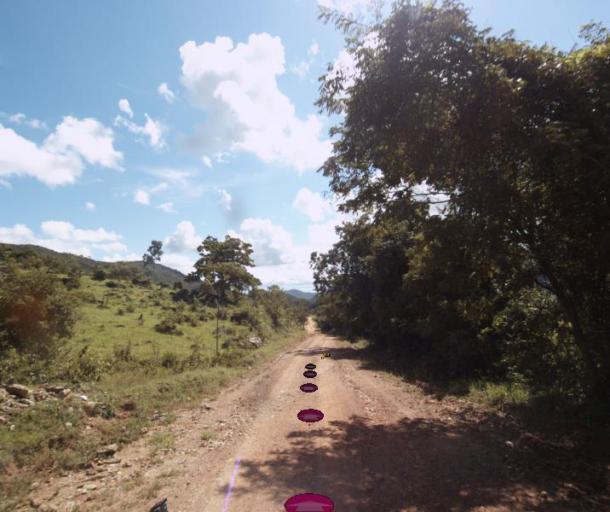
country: BR
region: Goias
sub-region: Pirenopolis
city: Pirenopolis
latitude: -15.7829
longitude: -48.9494
